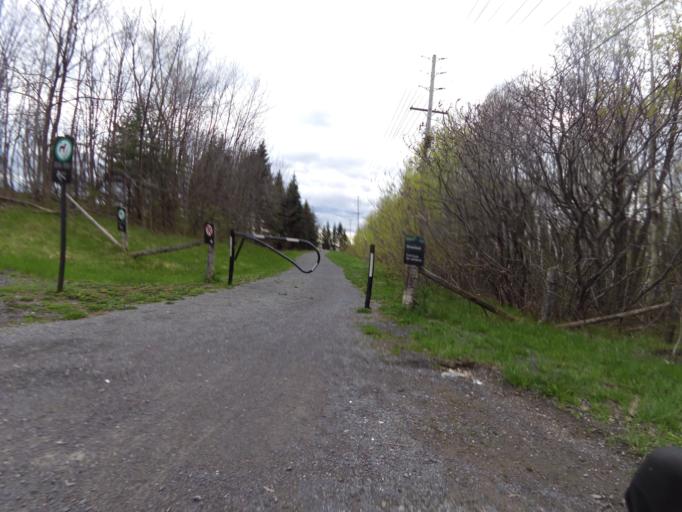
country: CA
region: Ontario
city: Bells Corners
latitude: 45.3180
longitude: -75.7894
